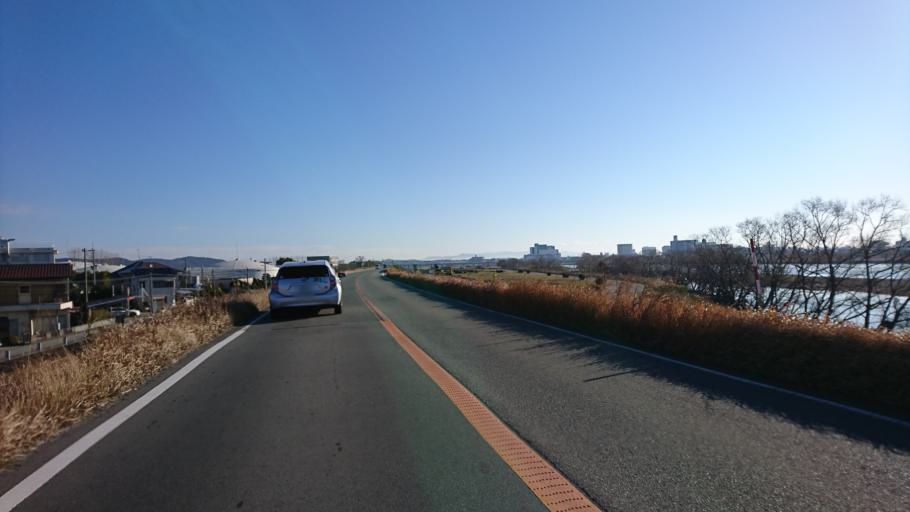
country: JP
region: Hyogo
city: Kakogawacho-honmachi
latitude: 34.7725
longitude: 134.8160
